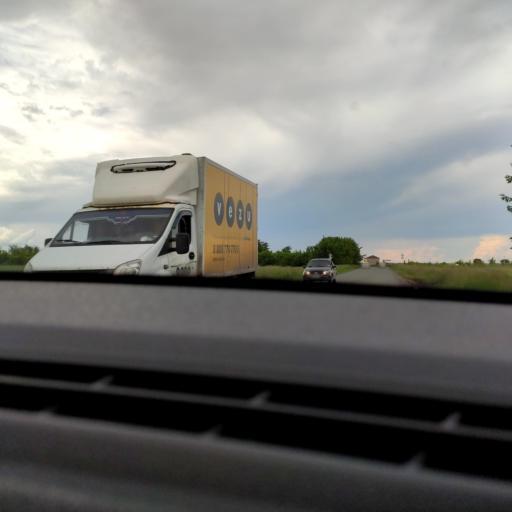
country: RU
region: Samara
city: Podstepki
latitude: 53.5230
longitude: 49.0976
